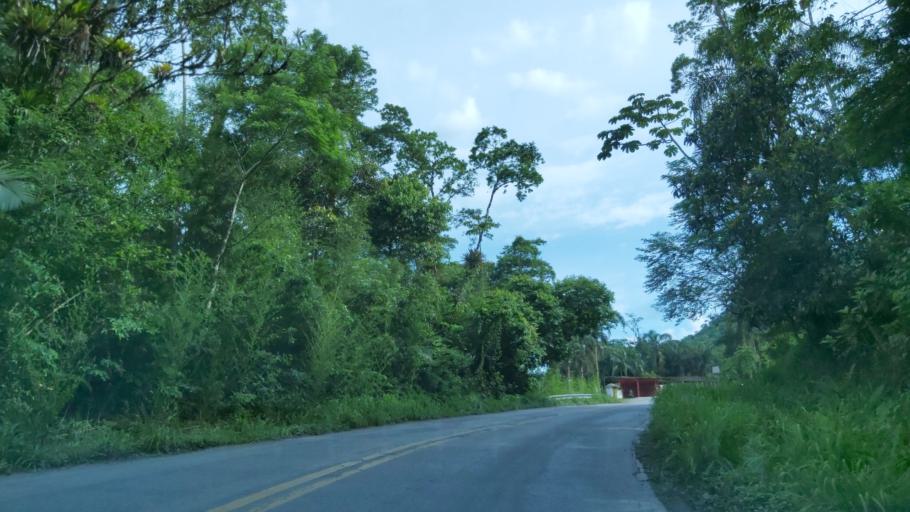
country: BR
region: Sao Paulo
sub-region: Miracatu
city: Miracatu
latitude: -24.0486
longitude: -47.5706
